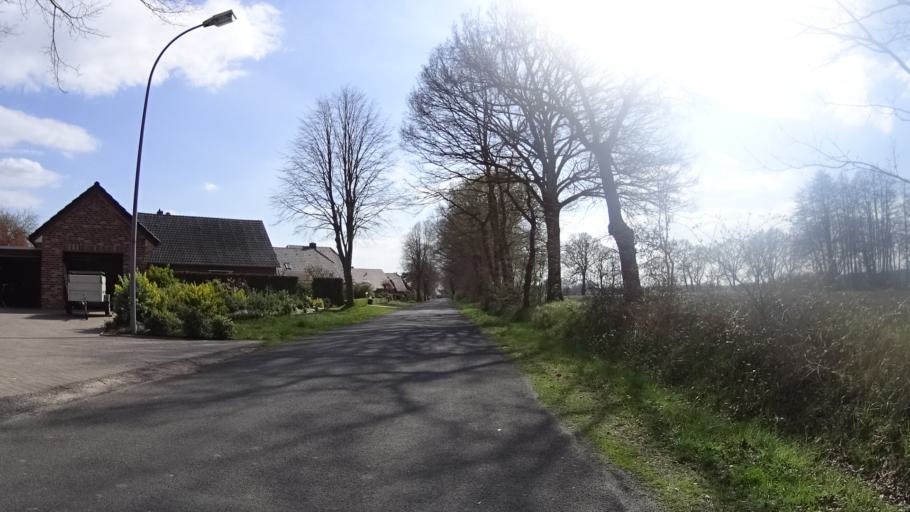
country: DE
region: Lower Saxony
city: Lehe
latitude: 53.0125
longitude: 7.3356
